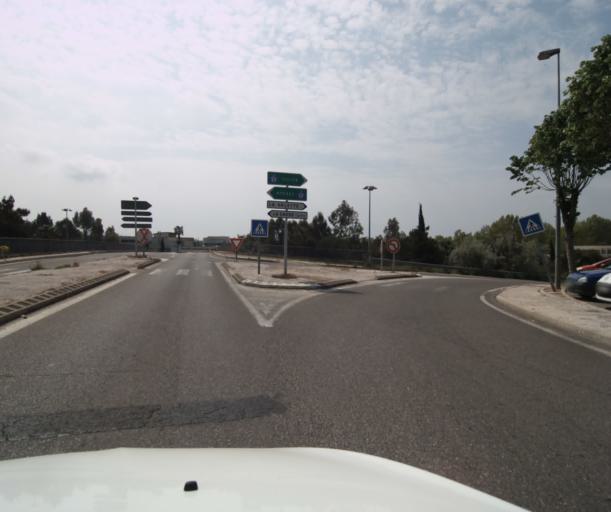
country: FR
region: Provence-Alpes-Cote d'Azur
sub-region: Departement du Var
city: La Garde
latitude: 43.1383
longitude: 6.0218
